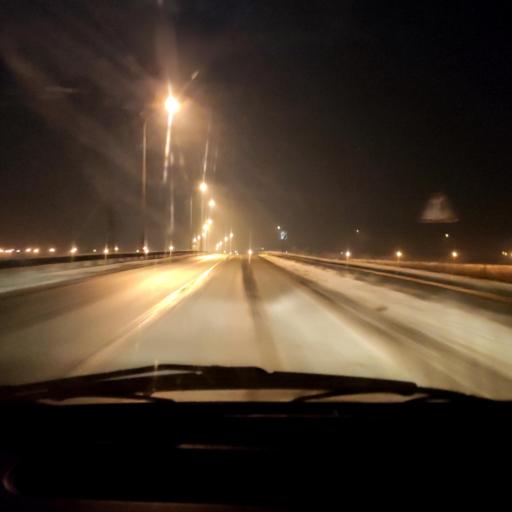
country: RU
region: Bashkortostan
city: Kabakovo
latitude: 54.6690
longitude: 56.1521
